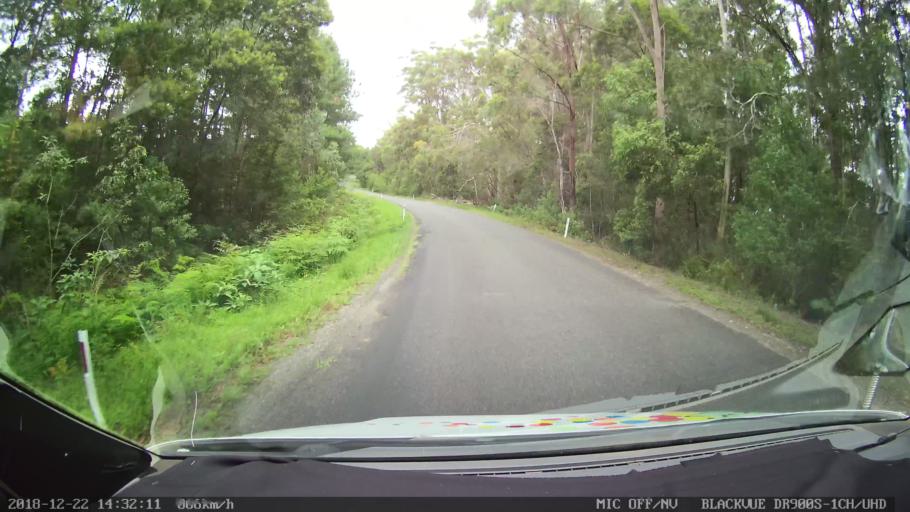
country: AU
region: New South Wales
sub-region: Bellingen
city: Dorrigo
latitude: -30.1013
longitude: 152.6274
